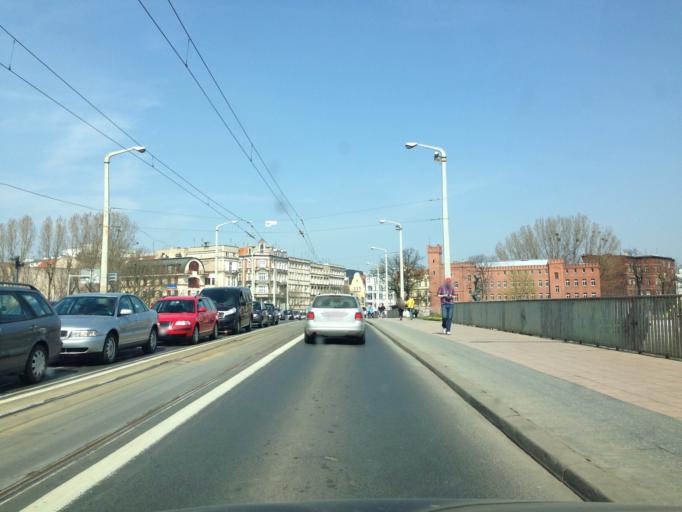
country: PL
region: Lower Silesian Voivodeship
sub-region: Powiat wroclawski
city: Wroclaw
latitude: 51.1146
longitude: 17.0341
